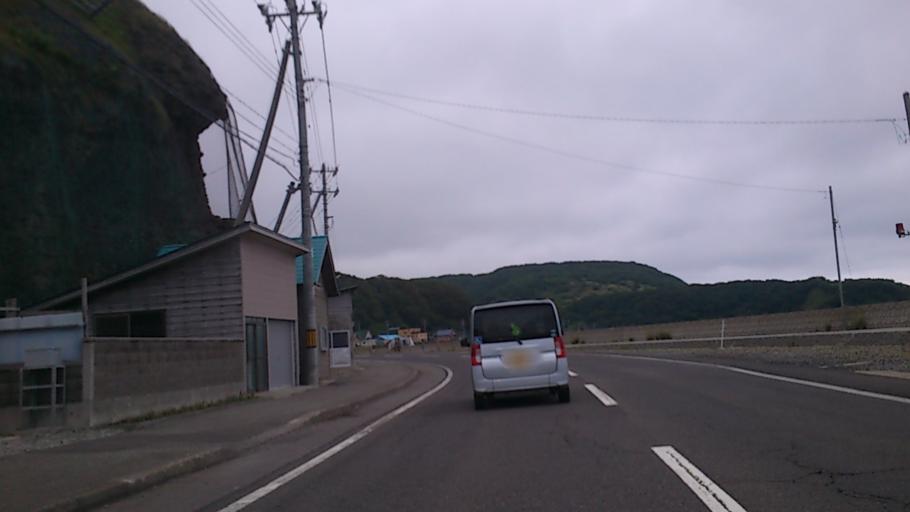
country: JP
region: Hokkaido
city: Iwanai
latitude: 42.7291
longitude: 140.0800
